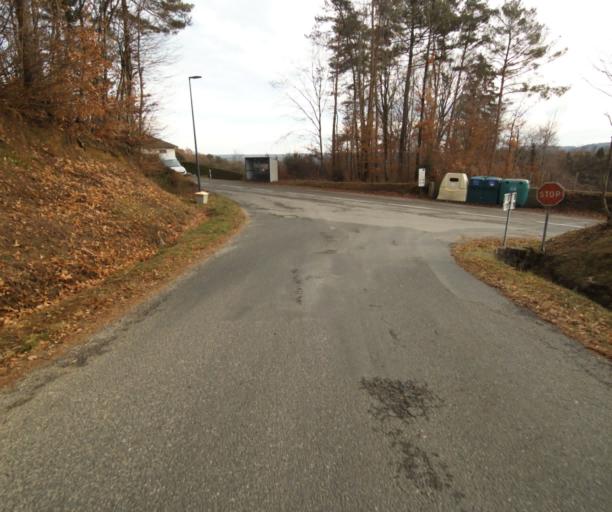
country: FR
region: Limousin
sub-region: Departement de la Correze
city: Chameyrat
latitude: 45.2578
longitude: 1.7034
